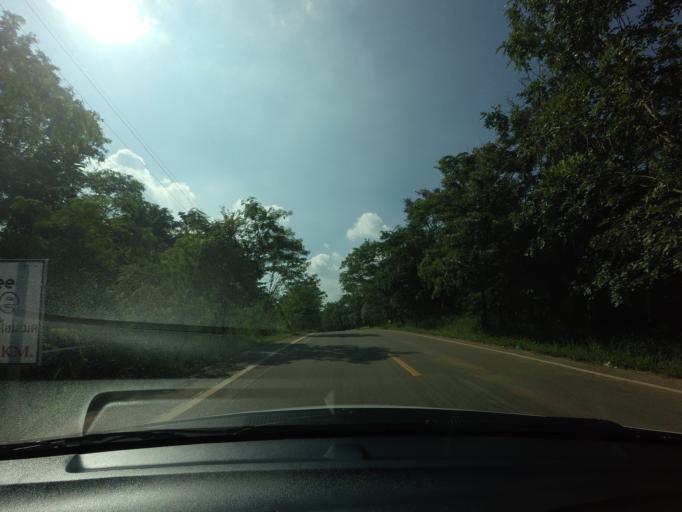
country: TH
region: Nakhon Ratchasima
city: Wang Nam Khiao
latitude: 14.4680
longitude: 101.6319
